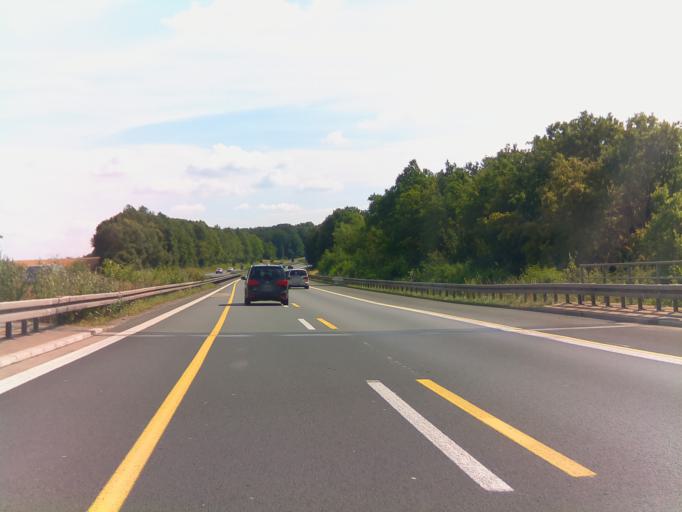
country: DE
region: Bavaria
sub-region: Regierungsbezirk Unterfranken
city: Arnstein
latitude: 49.9601
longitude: 10.0311
